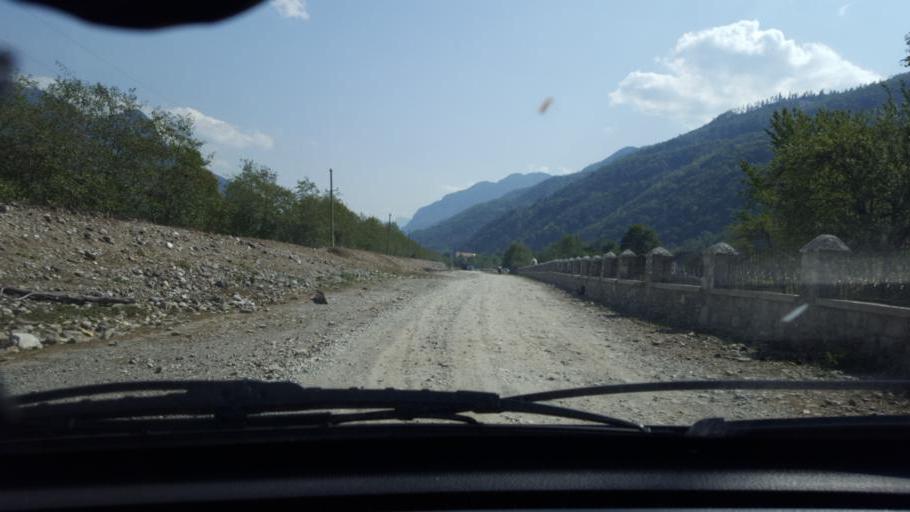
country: ME
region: Andrijevica
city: Andrijevica
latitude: 42.5932
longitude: 19.6831
